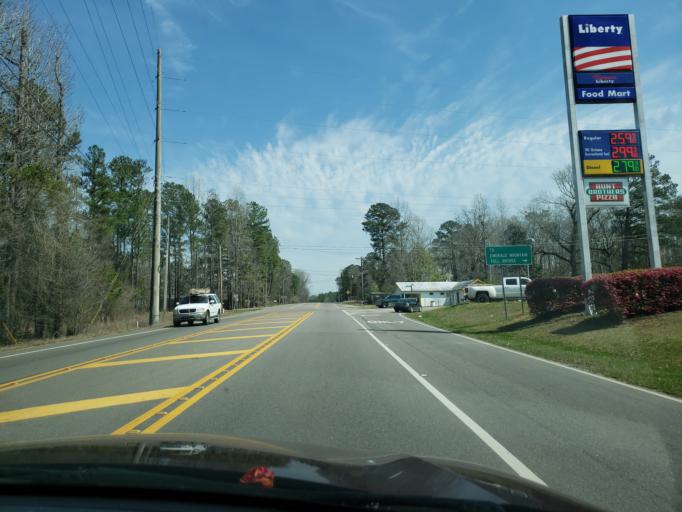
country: US
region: Alabama
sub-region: Elmore County
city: Wetumpka
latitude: 32.5565
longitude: -86.1534
